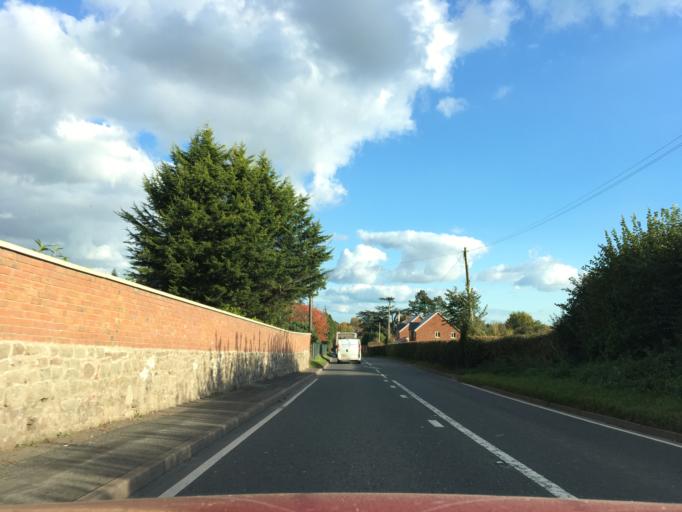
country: GB
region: England
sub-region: Herefordshire
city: Credenhill
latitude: 52.0723
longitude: -2.7825
